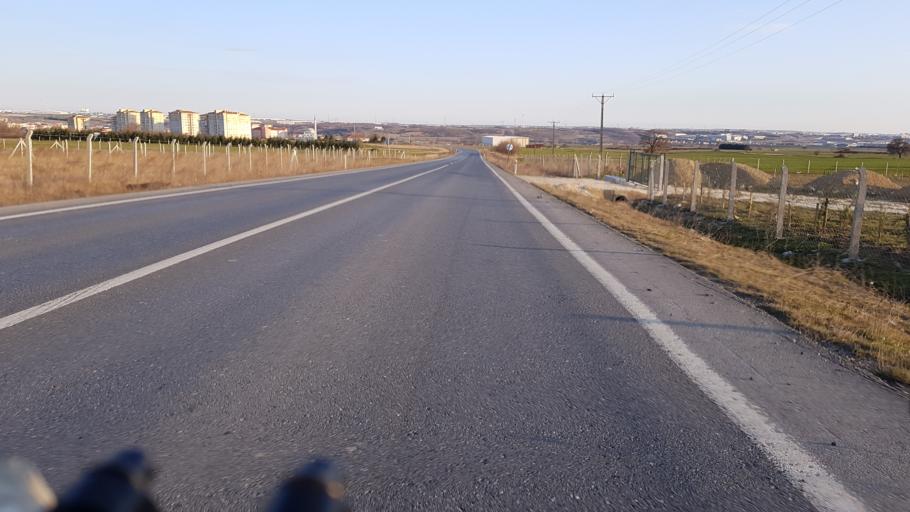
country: TR
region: Tekirdag
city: Velimese
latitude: 41.2583
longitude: 27.8600
